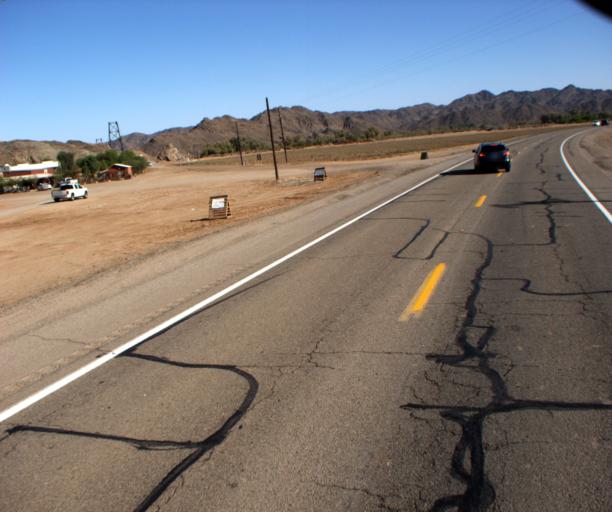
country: US
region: Arizona
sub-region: Yuma County
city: Fortuna Foothills
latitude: 32.7540
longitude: -114.4204
